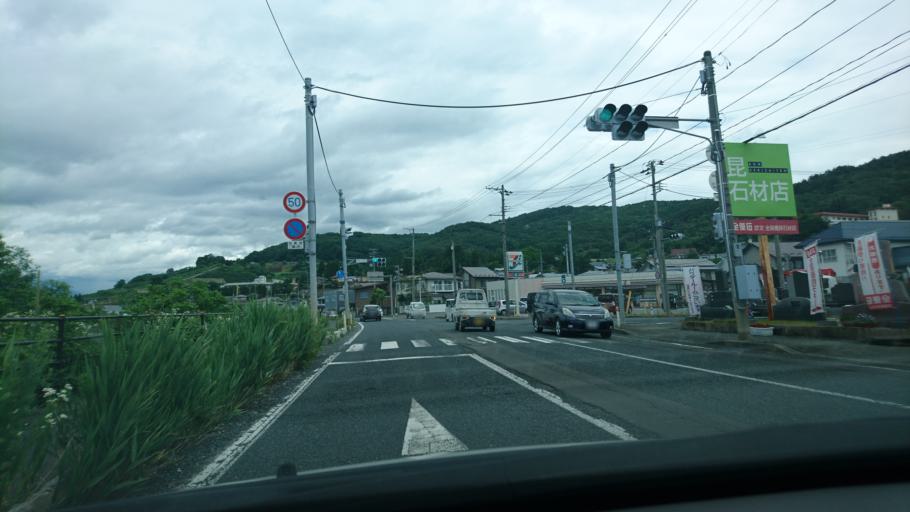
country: JP
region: Iwate
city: Morioka-shi
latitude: 39.6560
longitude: 141.1821
